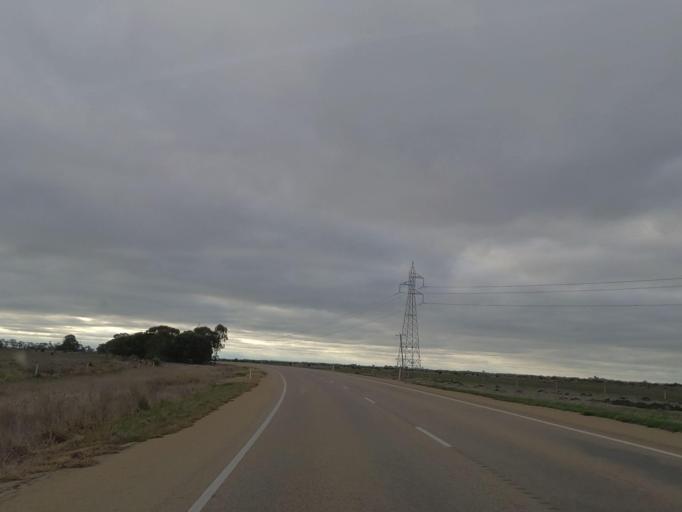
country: AU
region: Victoria
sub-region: Swan Hill
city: Swan Hill
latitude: -35.9066
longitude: 143.9473
